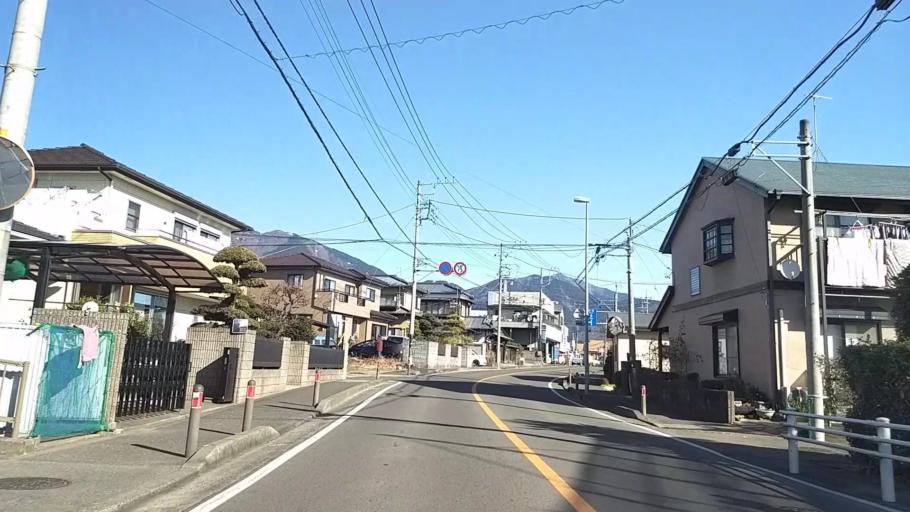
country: JP
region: Kanagawa
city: Hadano
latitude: 35.3902
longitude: 139.1794
